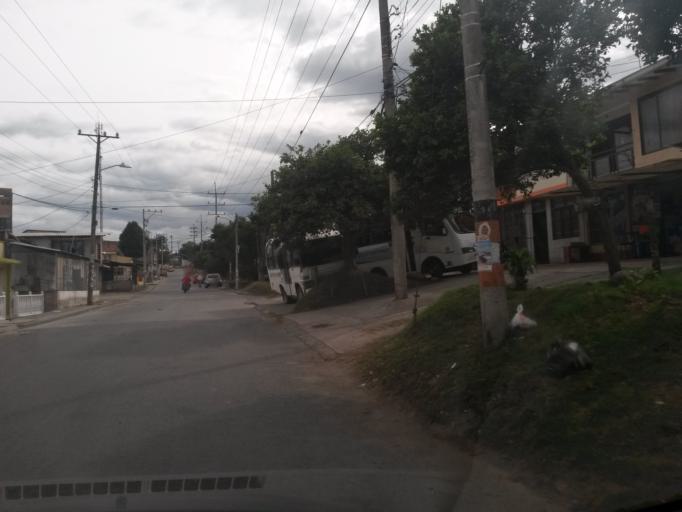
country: CO
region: Cauca
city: Popayan
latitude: 2.4538
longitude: -76.6304
